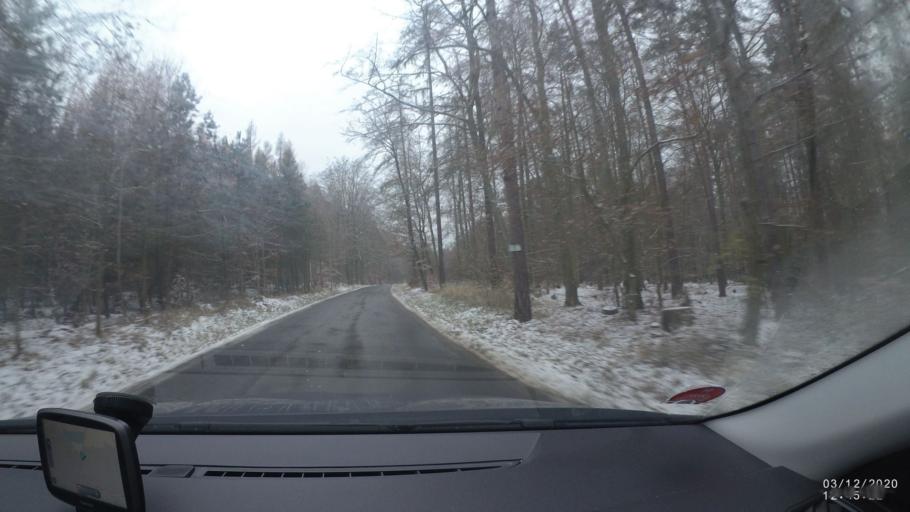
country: CZ
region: Central Bohemia
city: Revnicov
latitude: 50.1710
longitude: 13.8450
